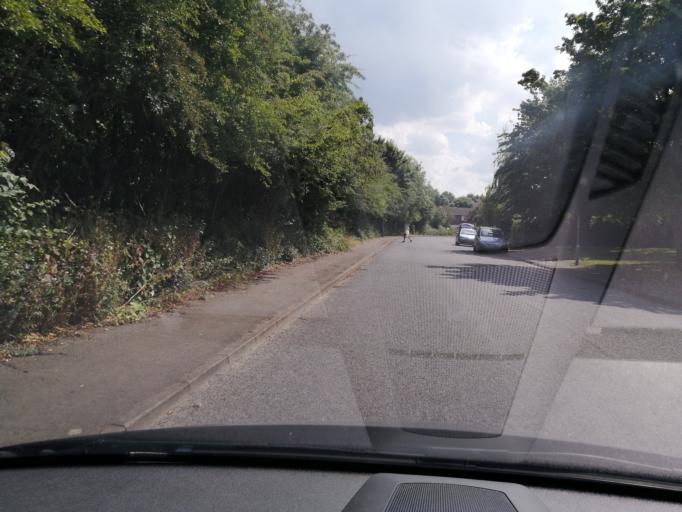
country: GB
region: England
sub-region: Cambridgeshire
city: Yaxley
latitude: 52.5196
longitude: -0.2414
